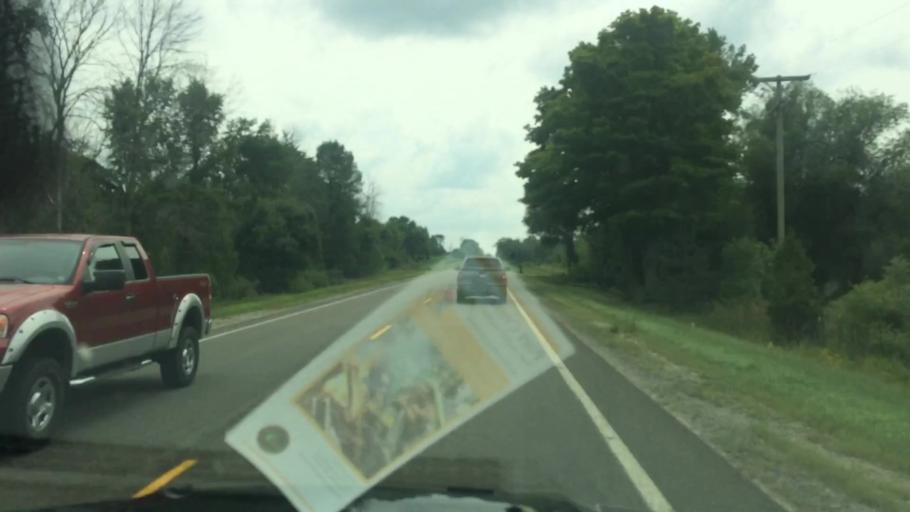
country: US
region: Michigan
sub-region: Tuscola County
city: Cass City
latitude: 43.6860
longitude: -83.0982
